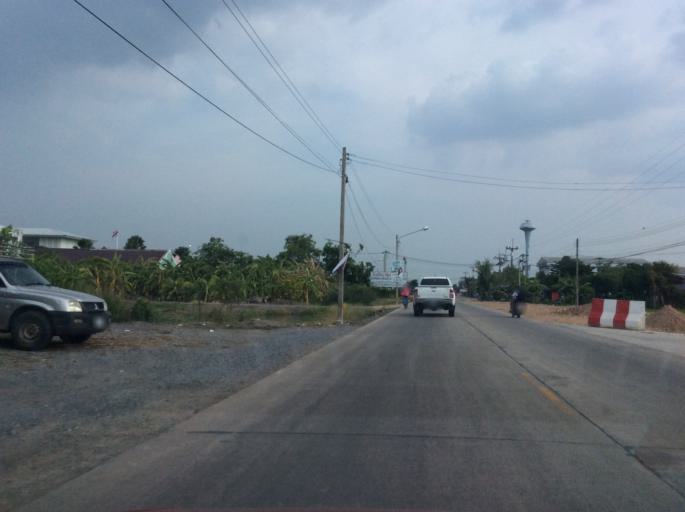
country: TH
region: Pathum Thani
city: Lam Luk Ka
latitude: 13.9672
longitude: 100.7259
